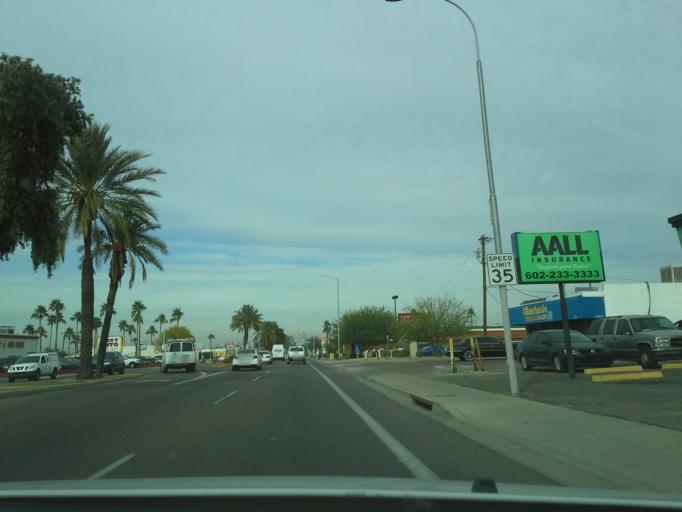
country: US
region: Arizona
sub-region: Maricopa County
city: Phoenix
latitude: 33.3971
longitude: -112.0733
